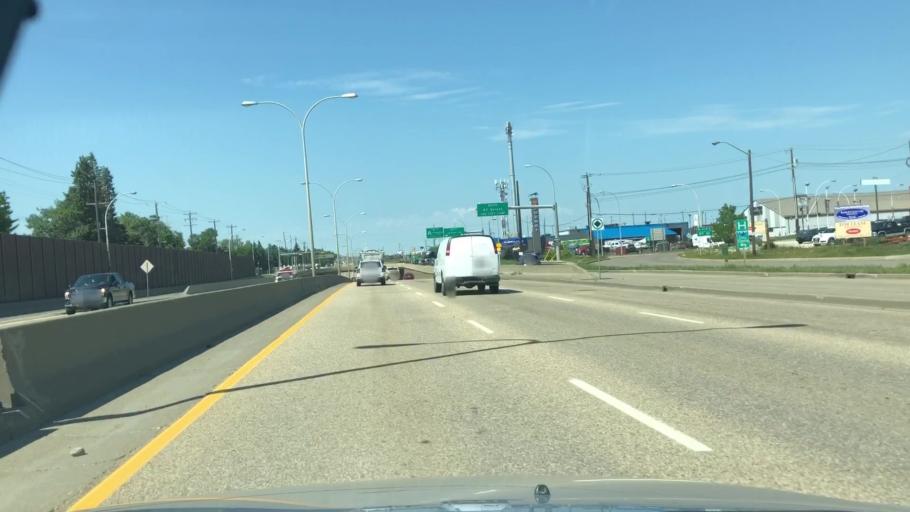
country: CA
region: Alberta
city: Edmonton
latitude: 53.5814
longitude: -113.4875
